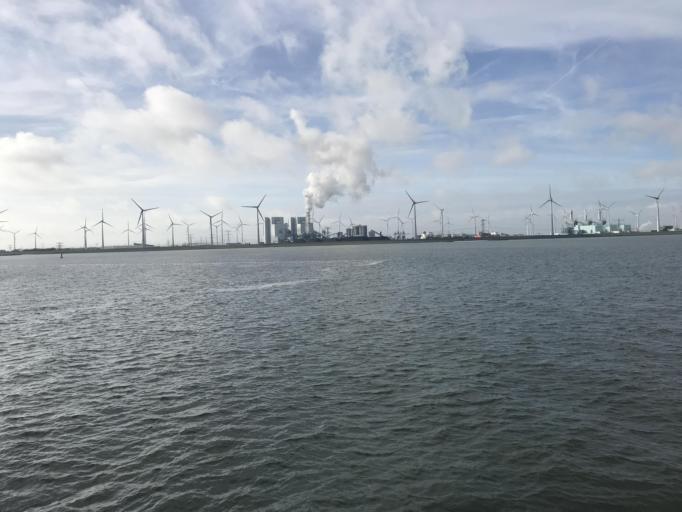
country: NL
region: Groningen
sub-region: Gemeente Delfzijl
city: Delfzijl
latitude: 53.4561
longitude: 6.8836
